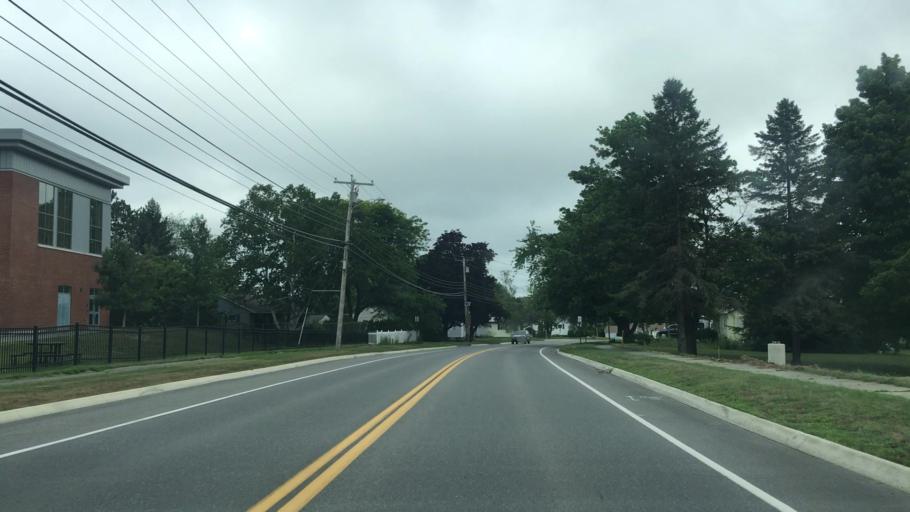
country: US
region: Maine
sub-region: Penobscot County
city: Brewer
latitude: 44.7765
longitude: -68.7691
